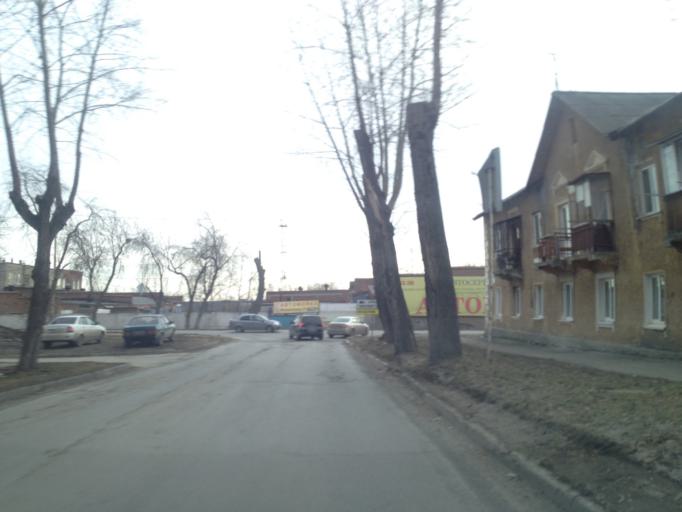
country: RU
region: Sverdlovsk
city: Shuvakish
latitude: 56.8679
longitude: 60.5254
